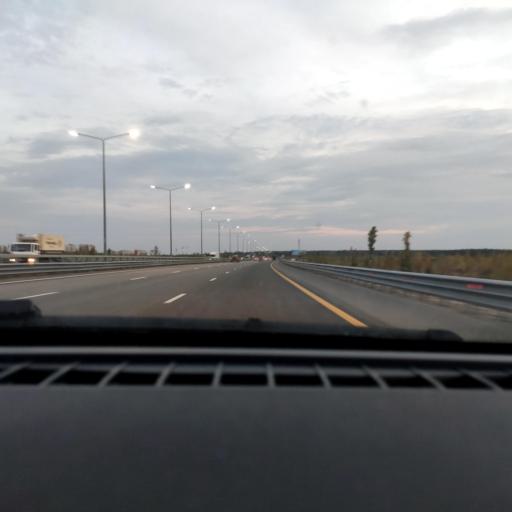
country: RU
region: Voronezj
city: Somovo
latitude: 51.7582
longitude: 39.3070
